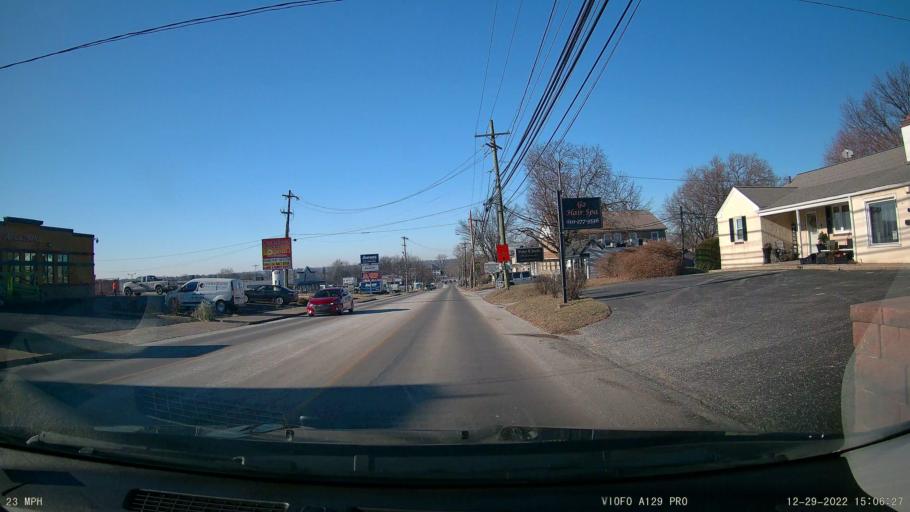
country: US
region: Pennsylvania
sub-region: Montgomery County
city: Norristown
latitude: 40.1323
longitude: -75.3290
